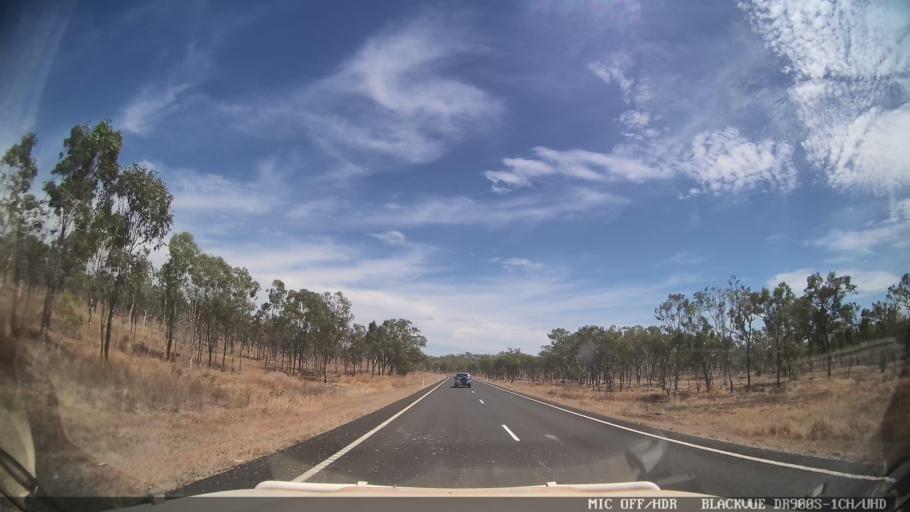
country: AU
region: Queensland
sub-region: Cook
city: Cooktown
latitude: -15.7590
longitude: 144.9960
